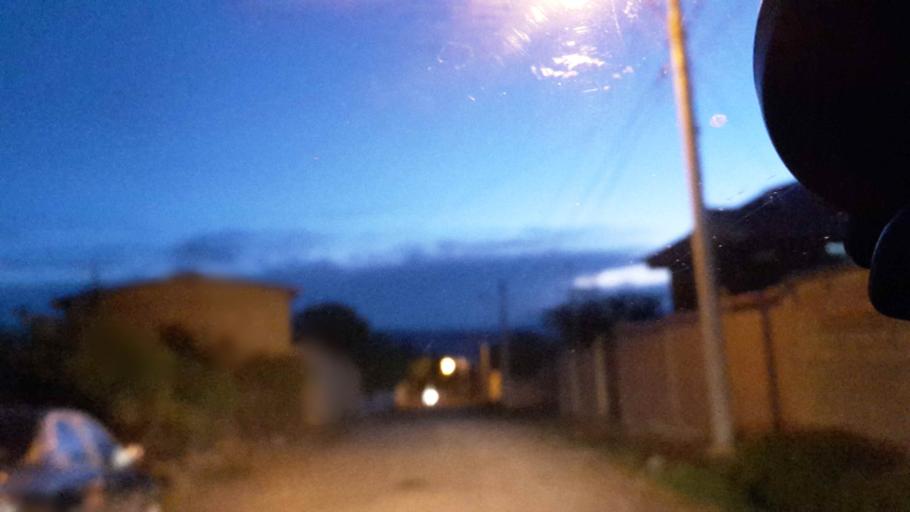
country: BO
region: Cochabamba
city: Cochabamba
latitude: -17.3287
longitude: -66.2167
